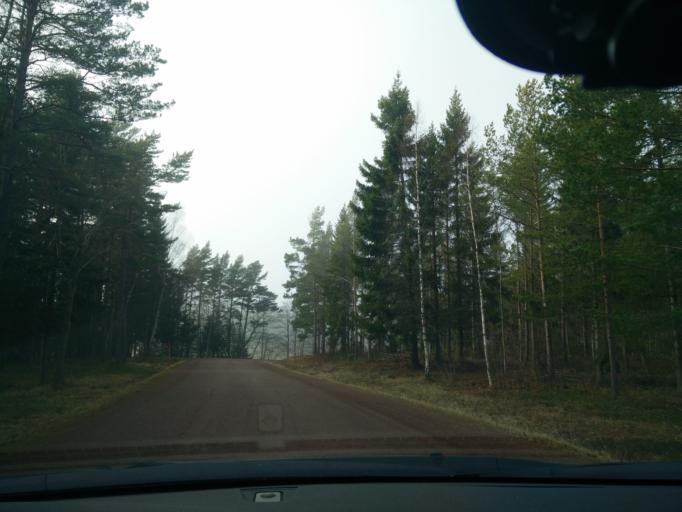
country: AX
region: Mariehamns stad
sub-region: Mariehamn
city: Mariehamn
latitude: 60.0969
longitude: 19.9124
